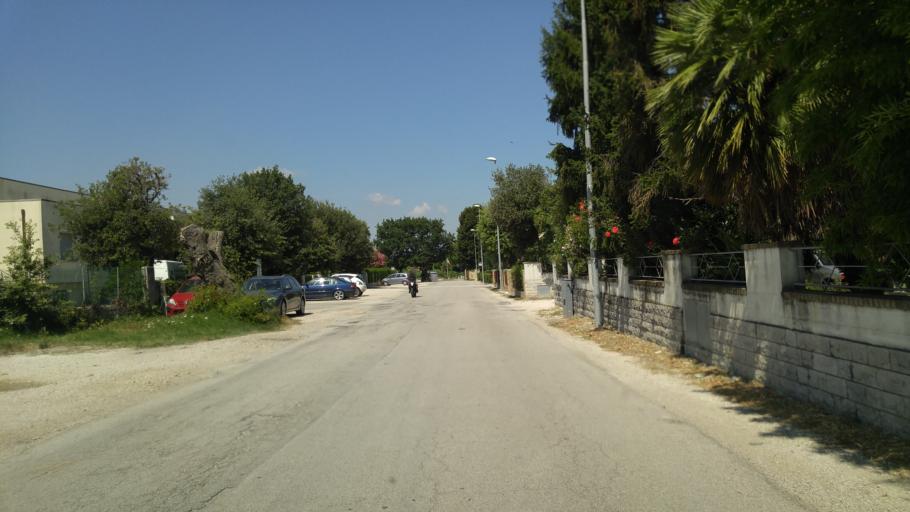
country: IT
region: The Marches
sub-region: Provincia di Pesaro e Urbino
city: Fano
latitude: 43.8255
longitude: 13.0394
